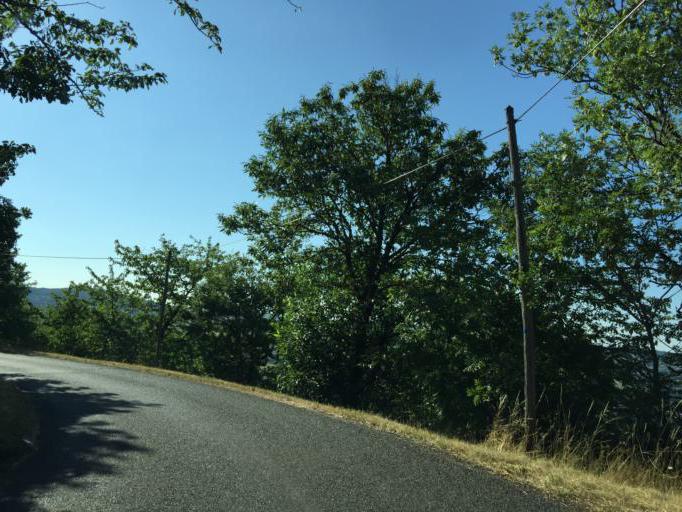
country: FR
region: Rhone-Alpes
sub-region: Departement de la Loire
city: Saint-Chamond
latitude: 45.4467
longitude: 4.4997
